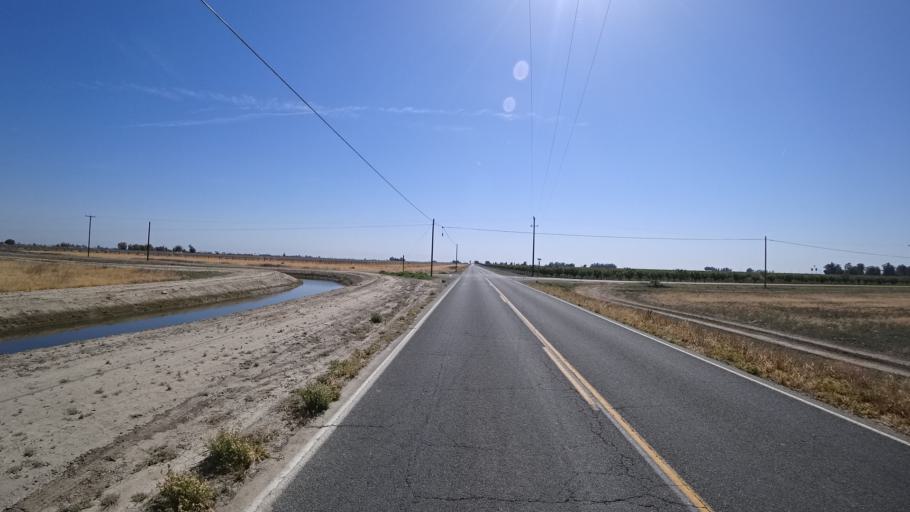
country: US
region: California
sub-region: Kings County
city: Stratford
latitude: 36.2115
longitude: -119.7988
